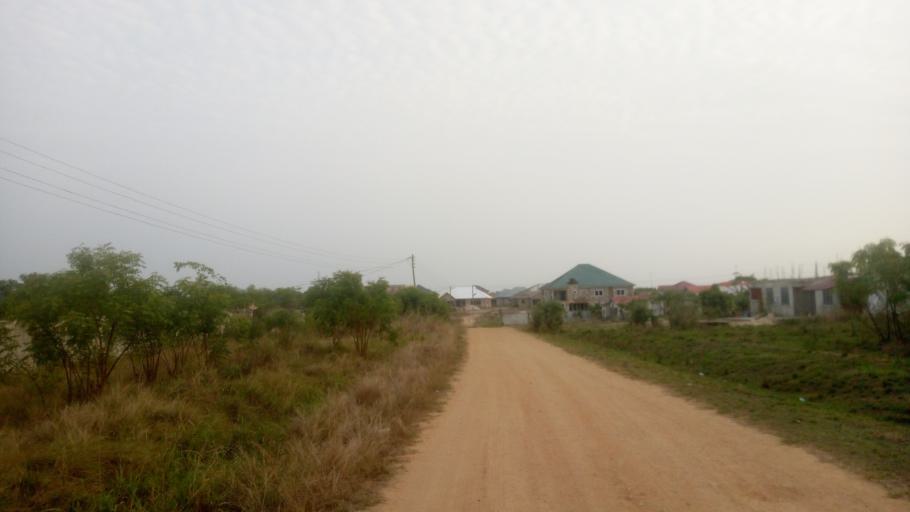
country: GH
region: Central
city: Winneba
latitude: 5.3813
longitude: -0.6287
